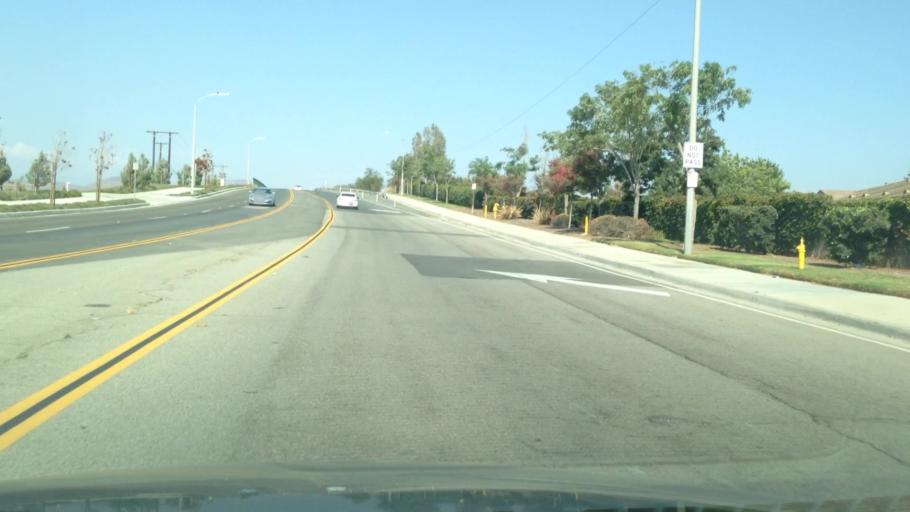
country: US
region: California
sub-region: Riverside County
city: Mira Loma
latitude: 33.9902
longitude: -117.5528
